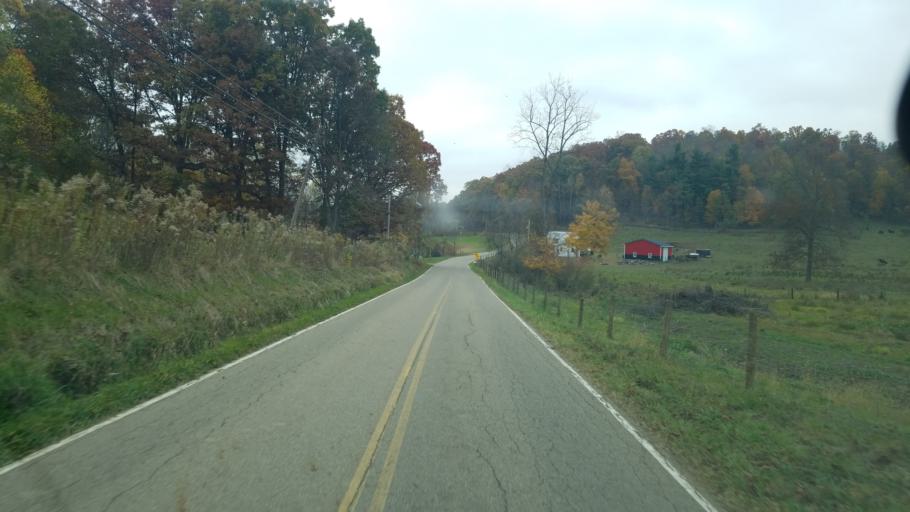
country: US
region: Ohio
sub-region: Licking County
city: Utica
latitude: 40.1644
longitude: -82.3845
